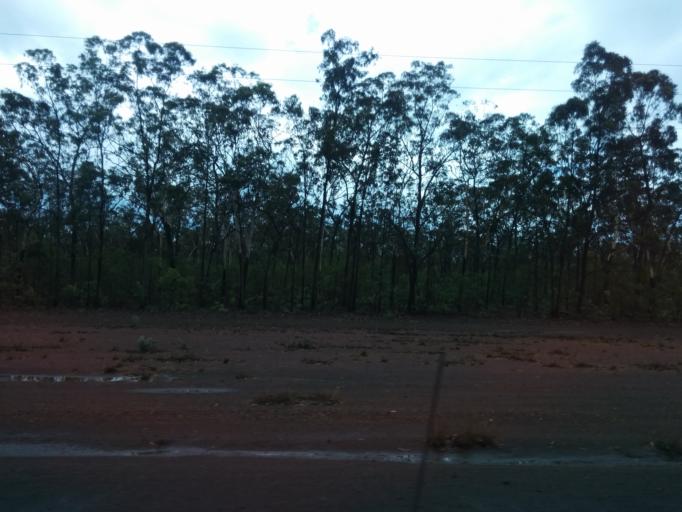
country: AU
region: Northern Territory
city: Alyangula
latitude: -13.9578
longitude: 136.4430
